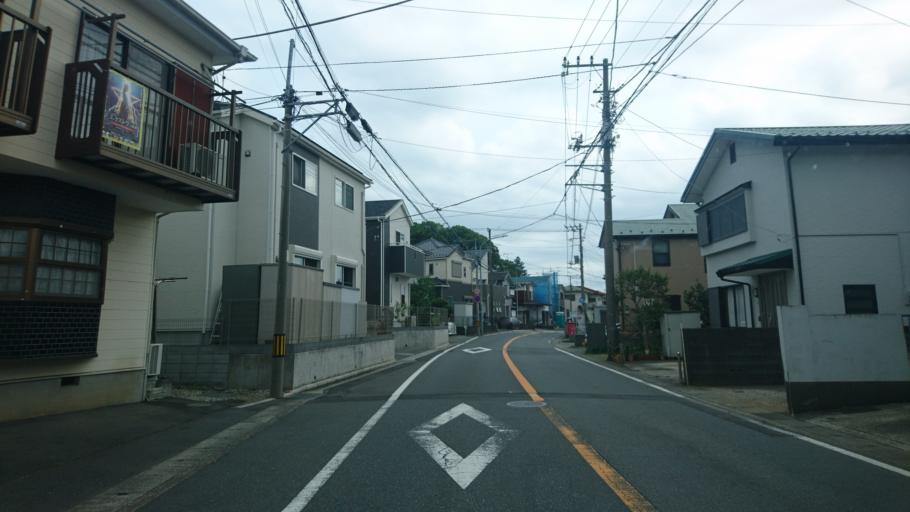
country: JP
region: Kanagawa
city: Minami-rinkan
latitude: 35.4155
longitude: 139.4797
